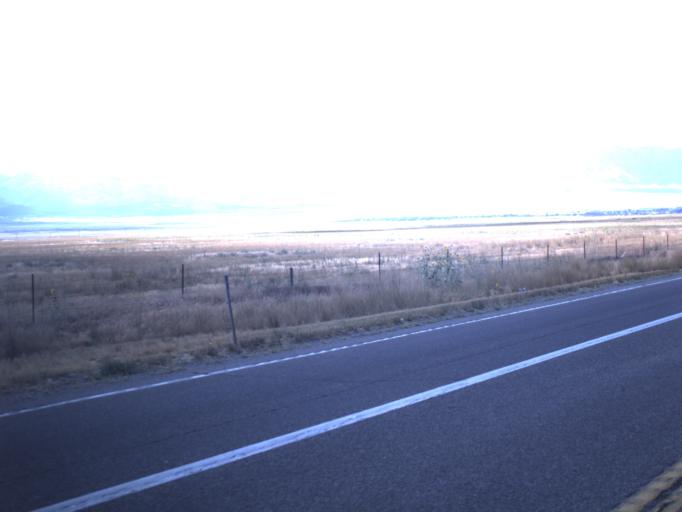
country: US
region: Utah
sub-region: Tooele County
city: Erda
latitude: 40.5712
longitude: -112.3770
